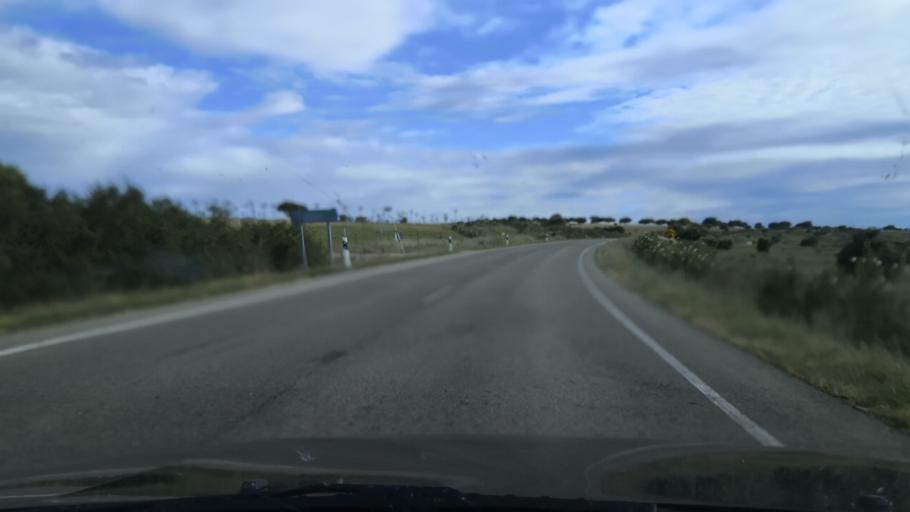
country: ES
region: Extremadura
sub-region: Provincia de Caceres
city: Perales del Puerto
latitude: 40.1159
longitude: -6.6703
